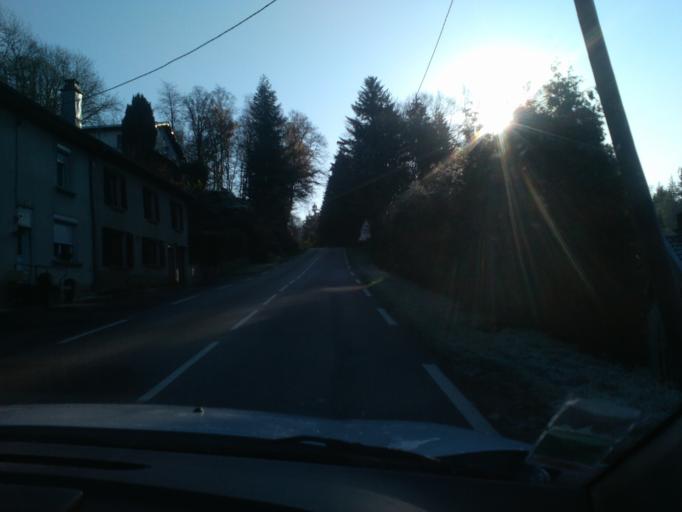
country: FR
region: Lorraine
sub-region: Departement des Vosges
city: Xertigny
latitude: 48.0433
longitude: 6.4090
